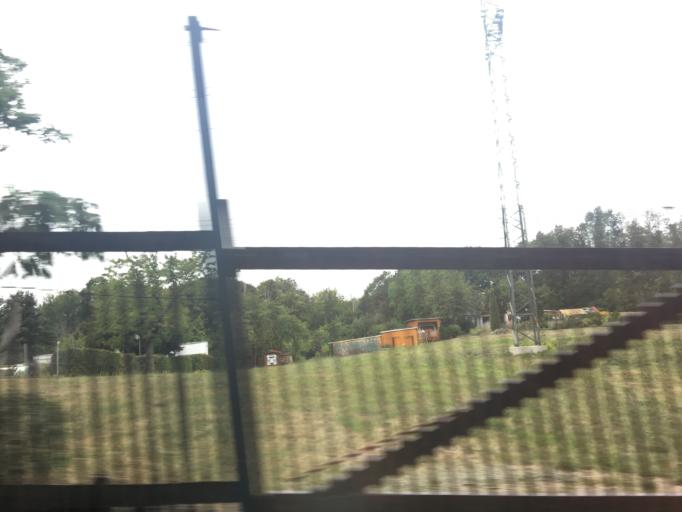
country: DE
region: Saxony
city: Coswig
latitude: 51.0866
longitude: 13.6042
